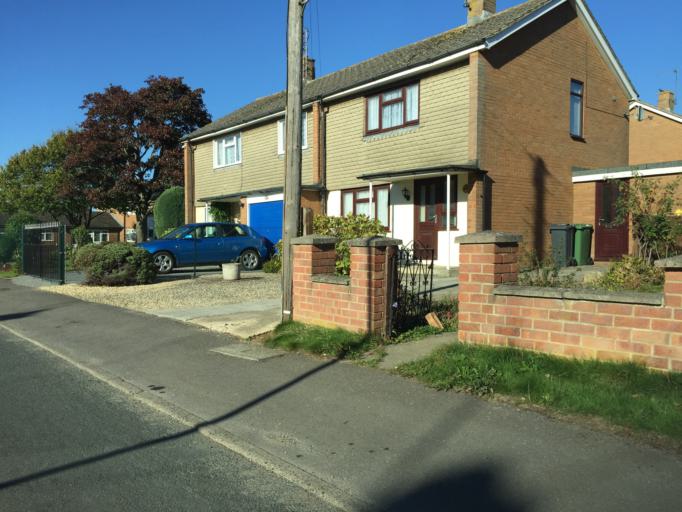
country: GB
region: England
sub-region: Gloucestershire
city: Stonehouse
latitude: 51.7456
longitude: -2.2892
